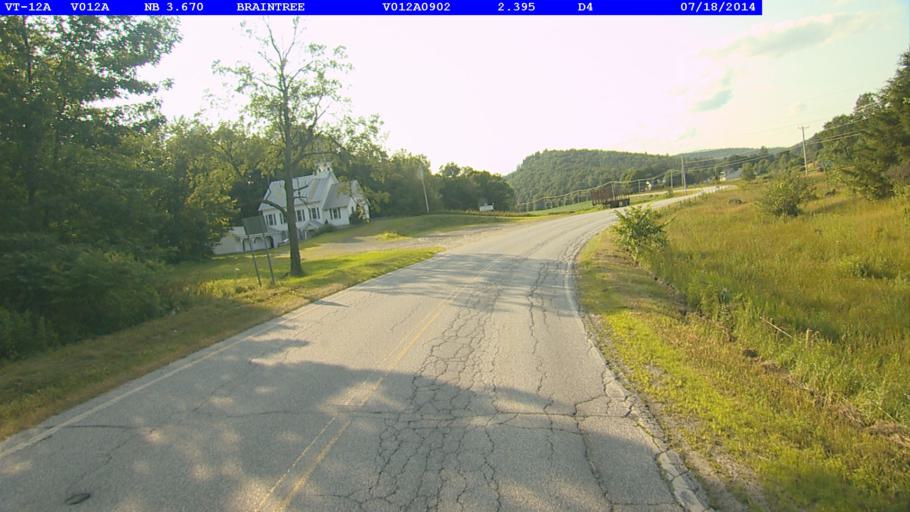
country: US
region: Vermont
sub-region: Orange County
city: Randolph
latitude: 43.9513
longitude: -72.7198
